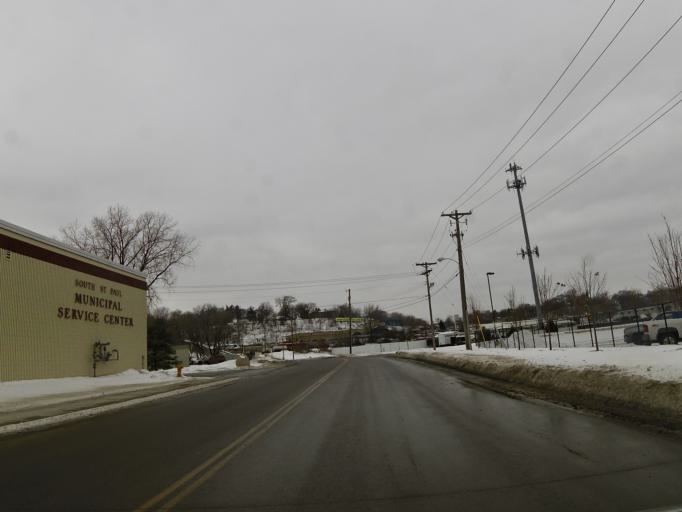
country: US
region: Minnesota
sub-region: Dakota County
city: South Saint Paul
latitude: 44.8736
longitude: -93.0262
